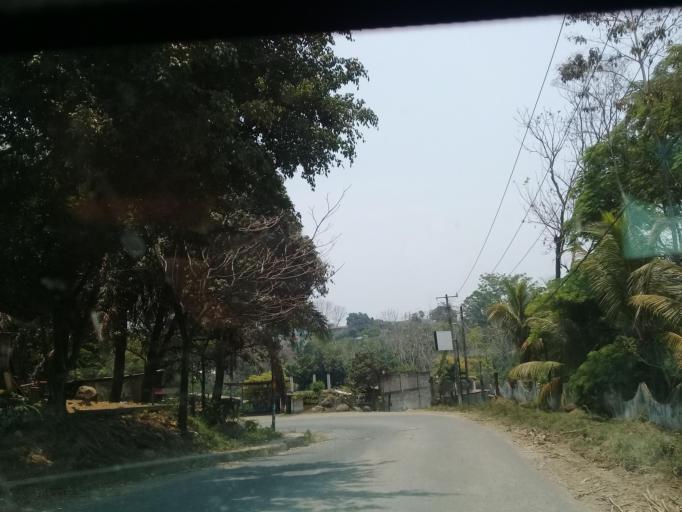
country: MX
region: Veracruz
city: Cosolapa
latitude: 18.5958
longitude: -96.6907
